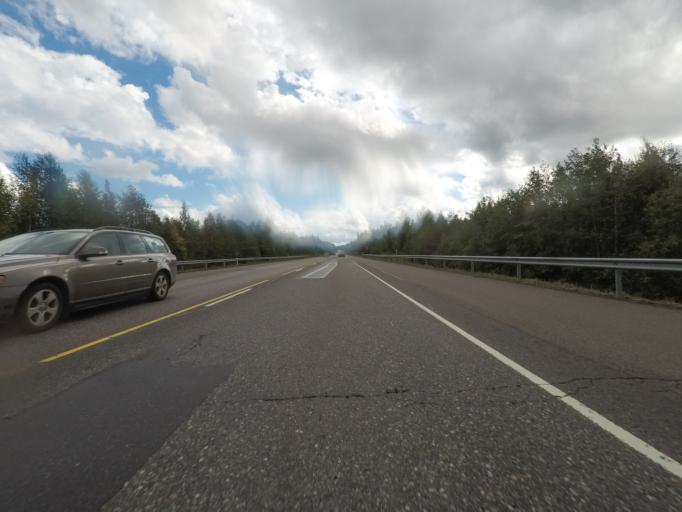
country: FI
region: Paijanne Tavastia
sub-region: Lahti
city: Heinola
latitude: 61.3260
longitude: 26.0412
